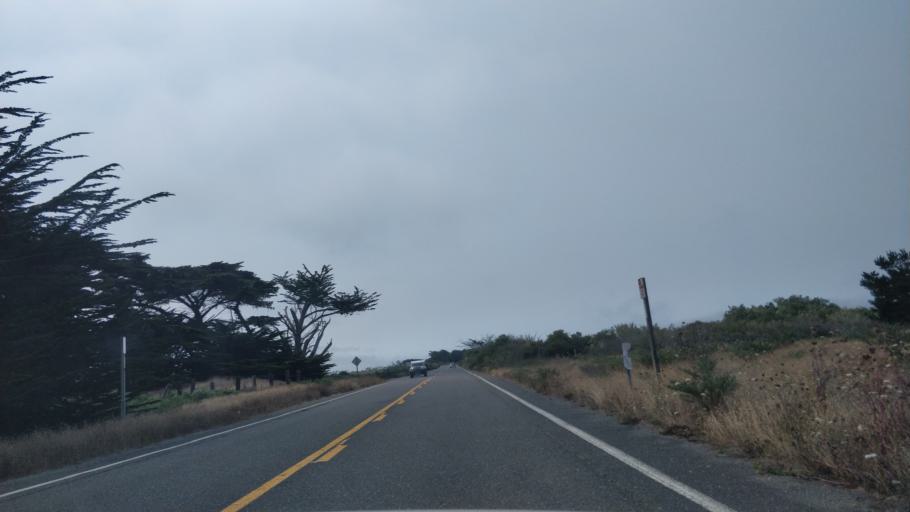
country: US
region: California
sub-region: Humboldt County
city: Bayview
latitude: 40.7786
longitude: -124.2087
